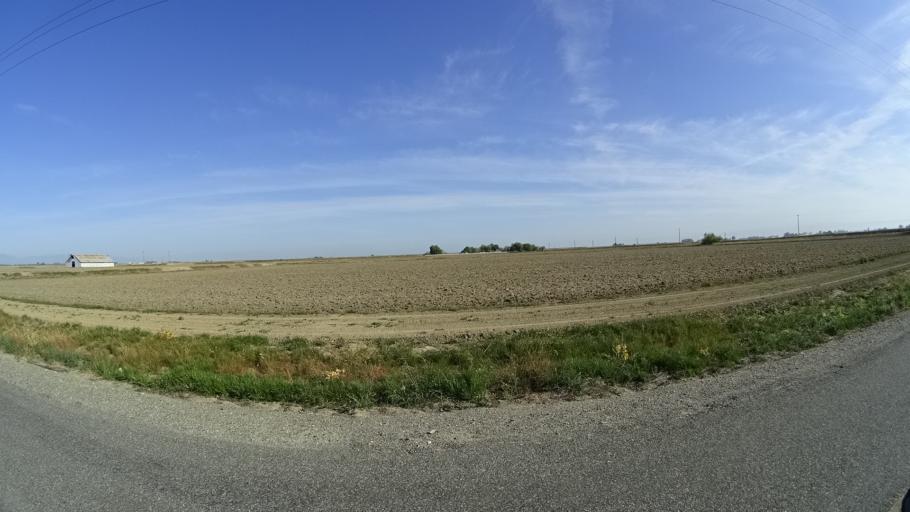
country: US
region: California
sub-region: Glenn County
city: Willows
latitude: 39.5532
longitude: -122.1337
